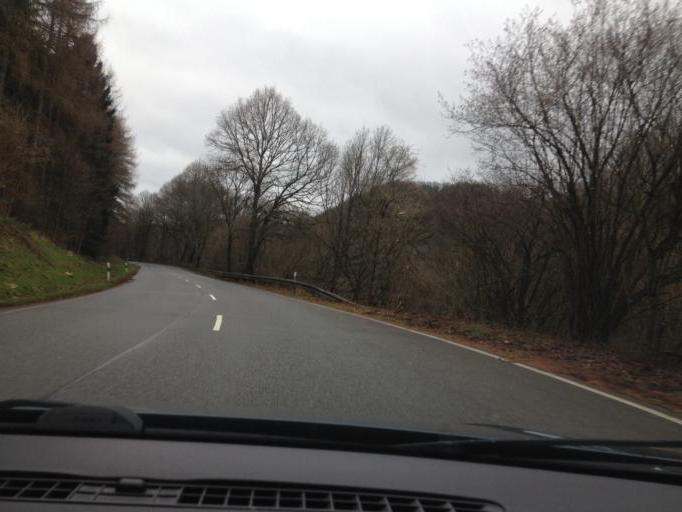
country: DE
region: Saarland
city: Hangard
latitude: 49.4071
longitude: 7.2271
